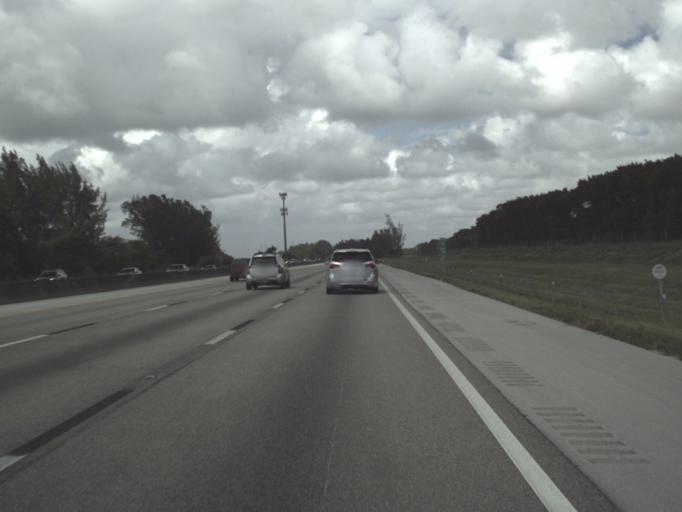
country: US
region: Florida
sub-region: Palm Beach County
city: Kings Point
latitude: 26.4195
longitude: -80.1715
